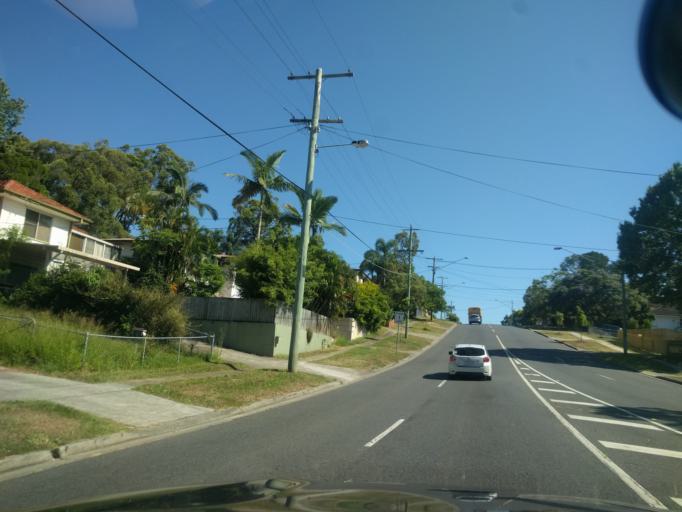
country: AU
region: Queensland
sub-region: Brisbane
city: Stafford Heights
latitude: -27.3958
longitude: 153.0105
